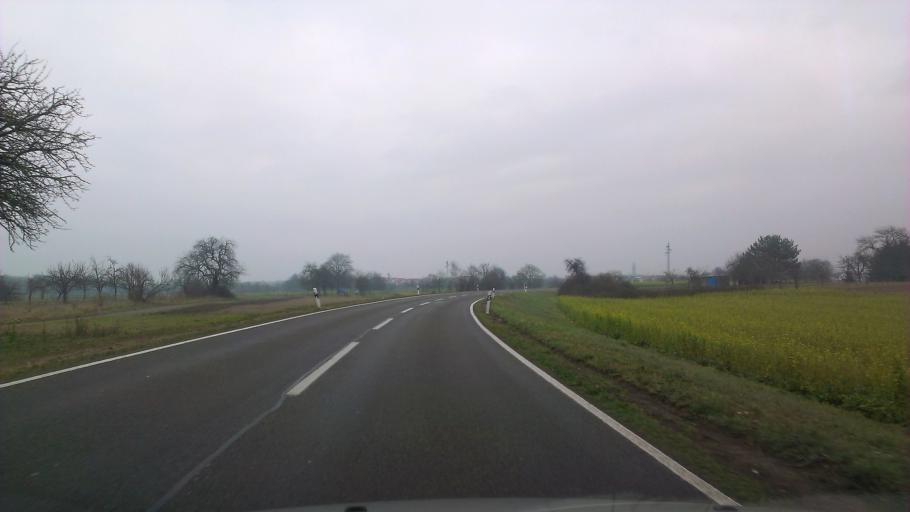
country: DE
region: Baden-Wuerttemberg
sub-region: Karlsruhe Region
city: Ubstadt-Weiher
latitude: 49.1728
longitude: 8.6064
